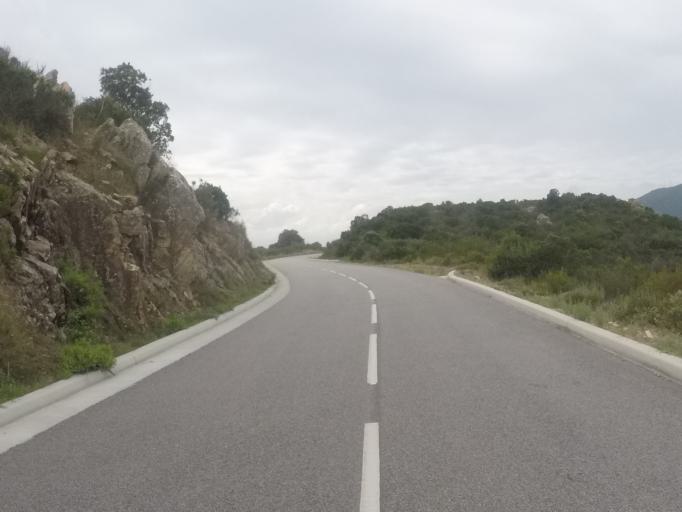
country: FR
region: Corsica
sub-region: Departement de la Corse-du-Sud
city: Pietrosella
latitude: 41.7752
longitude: 8.8187
